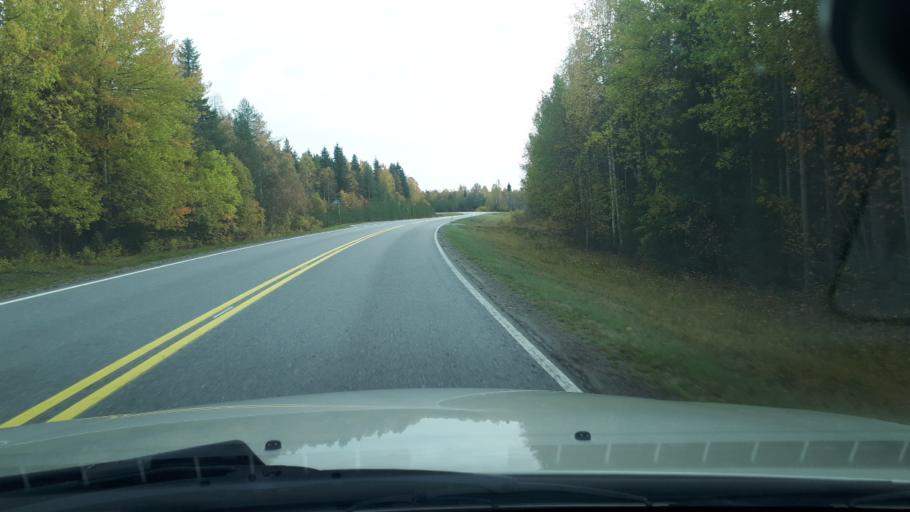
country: FI
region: Lapland
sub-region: Rovaniemi
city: Ranua
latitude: 66.0014
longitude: 26.2298
